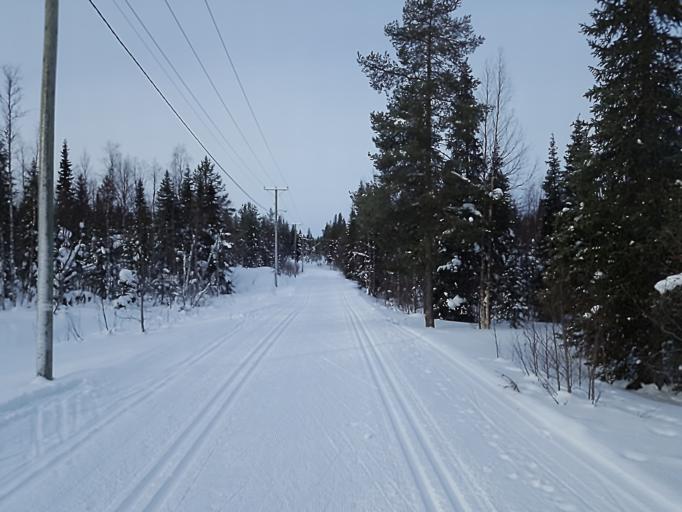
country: FI
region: Lapland
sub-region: Tunturi-Lappi
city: Kolari
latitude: 67.5944
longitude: 24.1671
